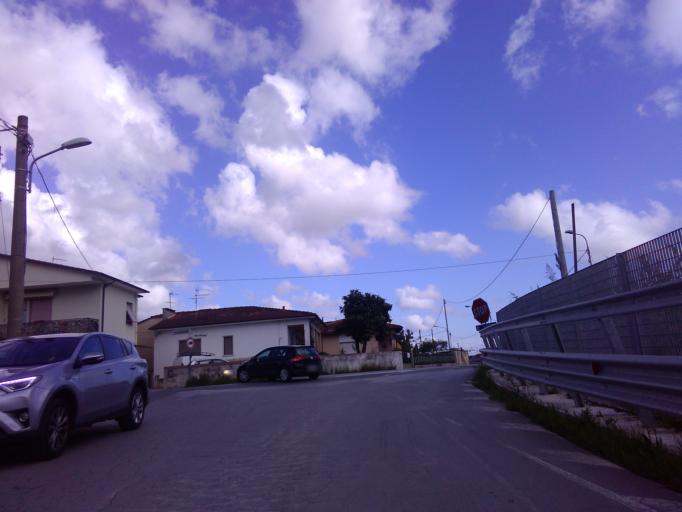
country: IT
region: Tuscany
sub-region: Provincia di Lucca
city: Strettoia
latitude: 43.9861
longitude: 10.1884
